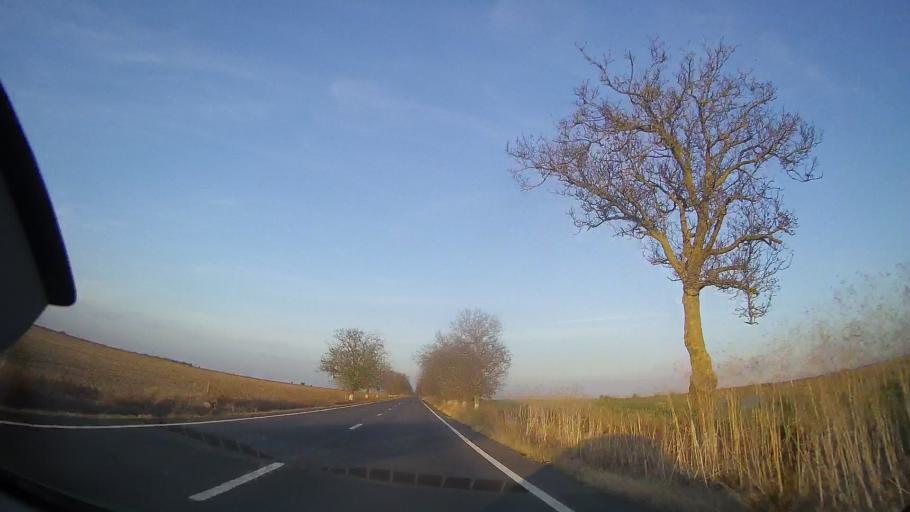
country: RO
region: Constanta
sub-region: Comuna Amzacea
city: Amzacea
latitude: 43.9470
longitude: 28.3781
